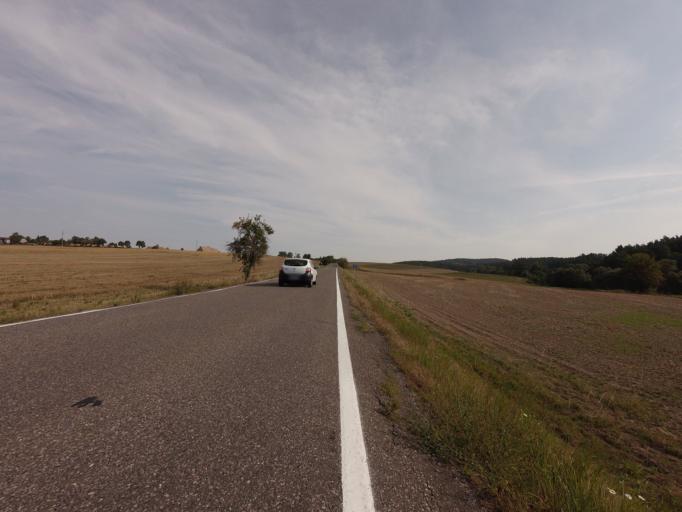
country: CZ
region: Jihocesky
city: Milevsko
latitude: 49.4762
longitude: 14.3652
